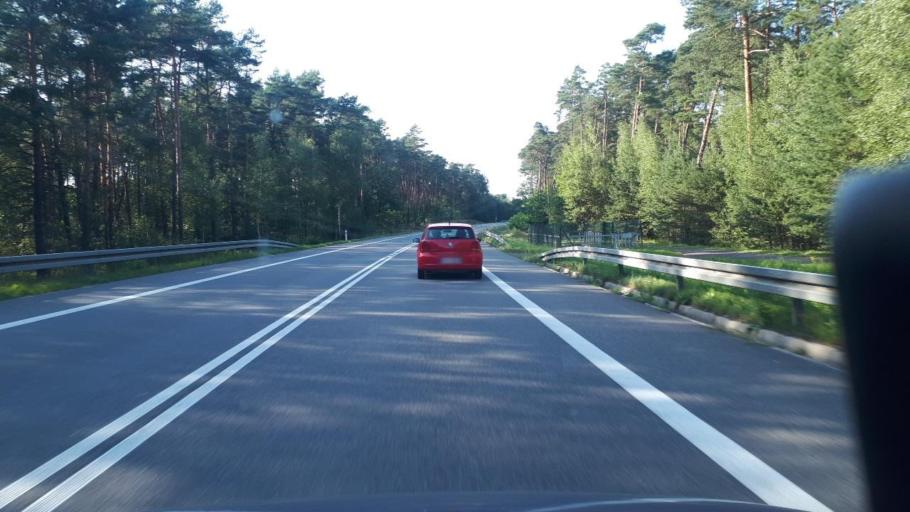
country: PL
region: Silesian Voivodeship
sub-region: Powiat lubliniecki
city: Lubliniec
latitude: 50.6587
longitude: 18.6565
